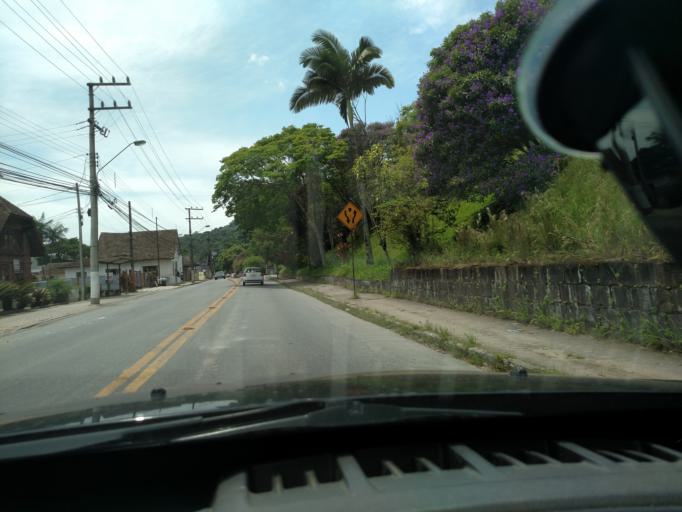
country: BR
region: Santa Catarina
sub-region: Blumenau
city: Blumenau
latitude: -26.9128
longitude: -49.0519
